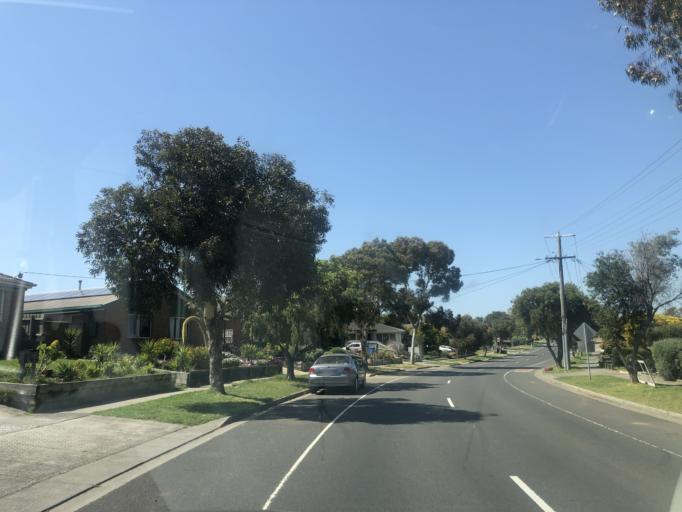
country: AU
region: Victoria
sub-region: Casey
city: Hallam
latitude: -38.0315
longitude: 145.2717
